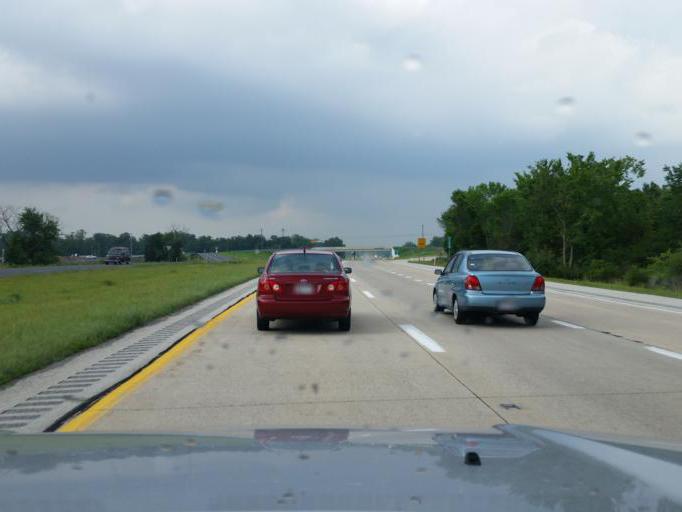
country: US
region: Pennsylvania
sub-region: Adams County
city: Gettysburg
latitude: 39.8866
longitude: -77.1839
